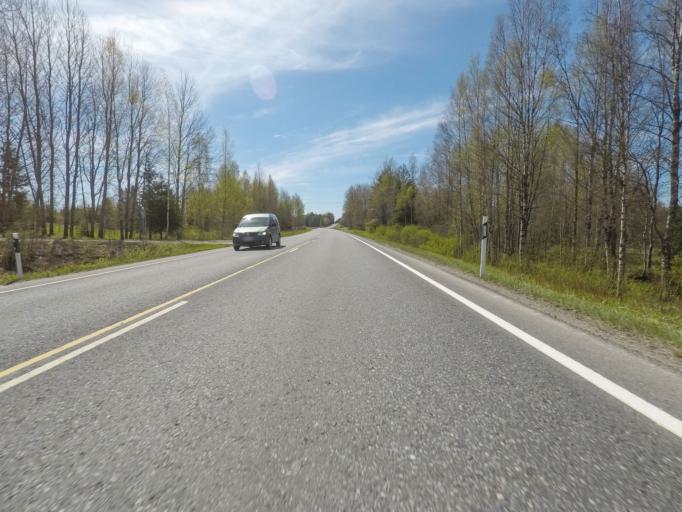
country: FI
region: Pirkanmaa
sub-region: Etelae-Pirkanmaa
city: Urjala
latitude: 61.0145
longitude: 23.4776
